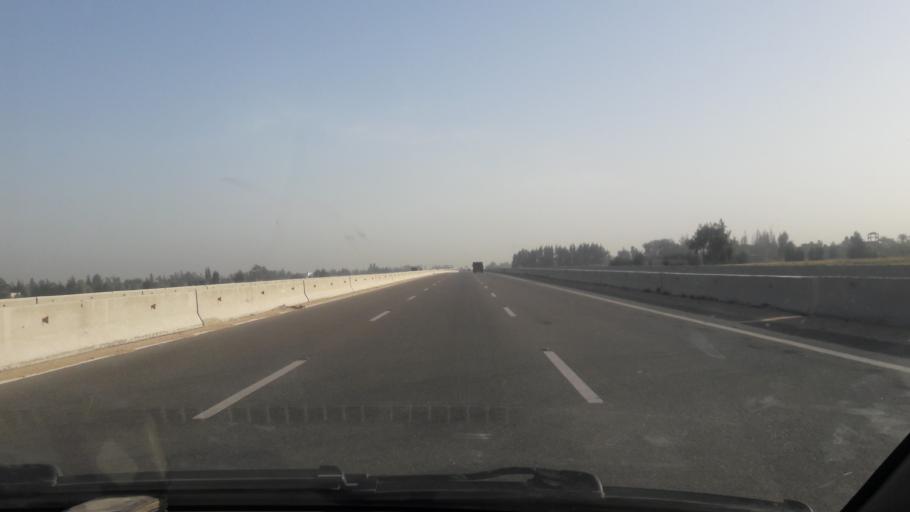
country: EG
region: Al Isma'iliyah
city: Ismailia
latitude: 30.7217
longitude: 32.1220
